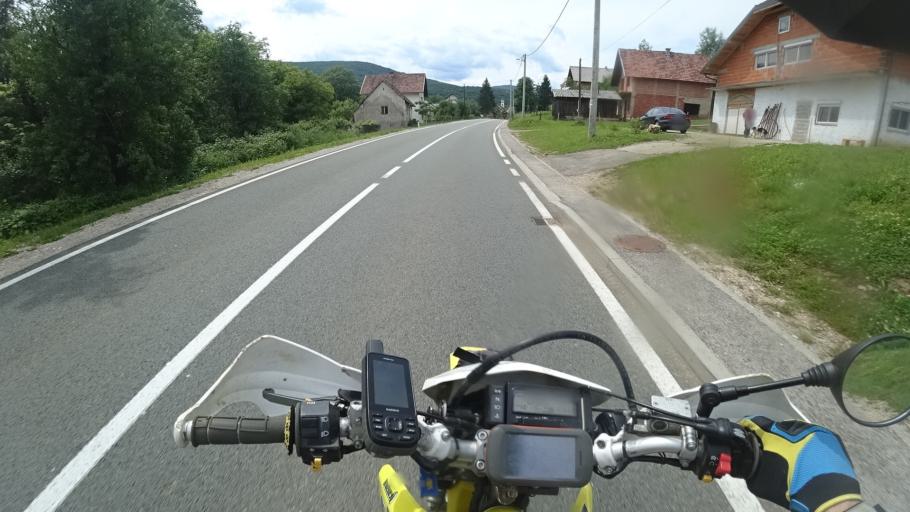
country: BA
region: Federation of Bosnia and Herzegovina
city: Izacic
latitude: 44.8786
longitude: 15.7164
